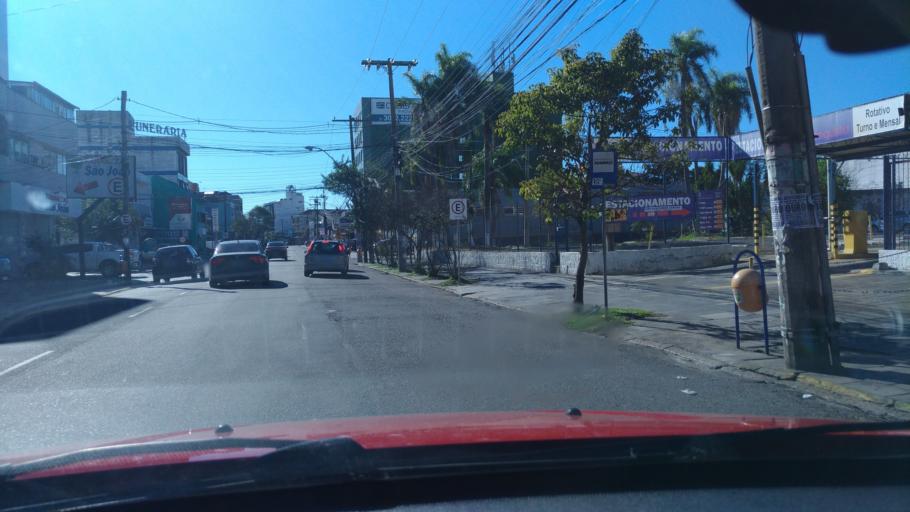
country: BR
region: Rio Grande do Sul
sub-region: Porto Alegre
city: Porto Alegre
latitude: -30.0106
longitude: -51.1705
